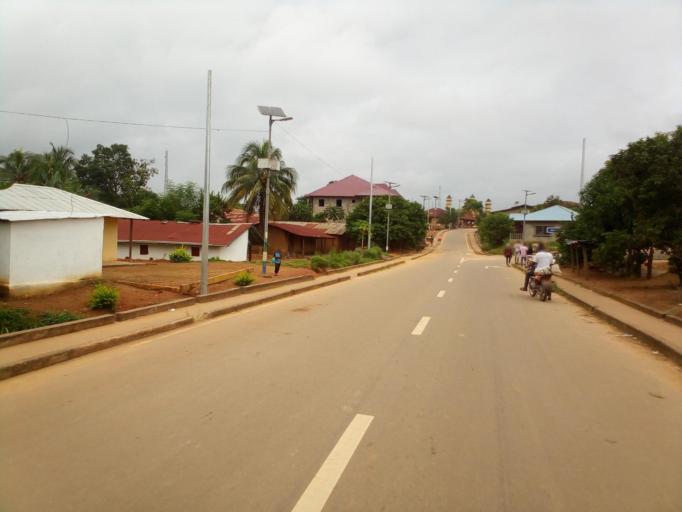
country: SL
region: Eastern Province
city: Kailahun
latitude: 8.2773
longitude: -10.5758
